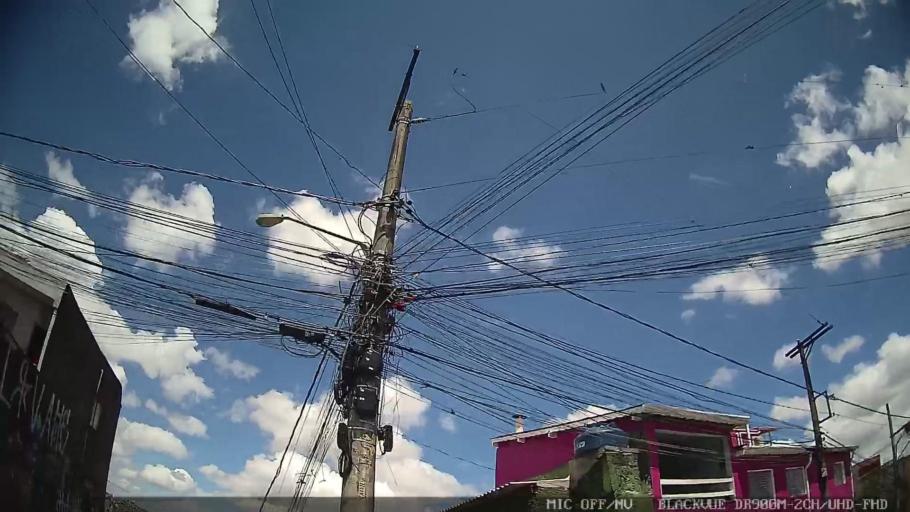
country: BR
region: Sao Paulo
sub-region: Diadema
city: Diadema
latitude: -23.6799
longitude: -46.6450
